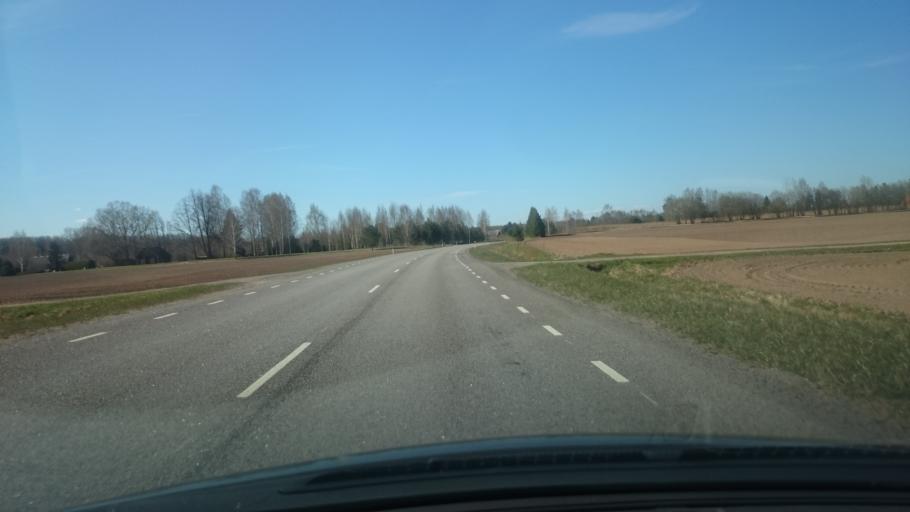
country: EE
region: Polvamaa
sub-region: Polva linn
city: Polva
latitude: 58.2459
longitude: 27.0045
